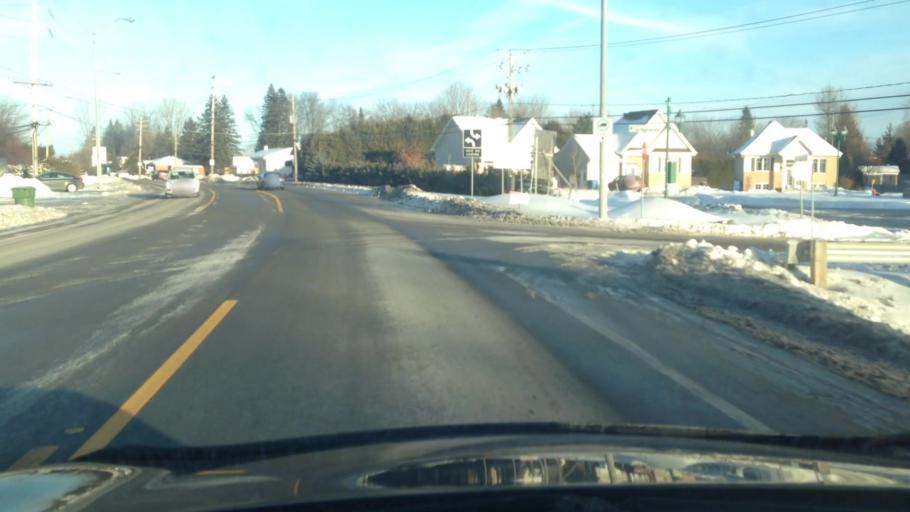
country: CA
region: Quebec
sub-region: Laurentides
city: Sainte-Sophie
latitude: 45.8206
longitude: -73.8954
